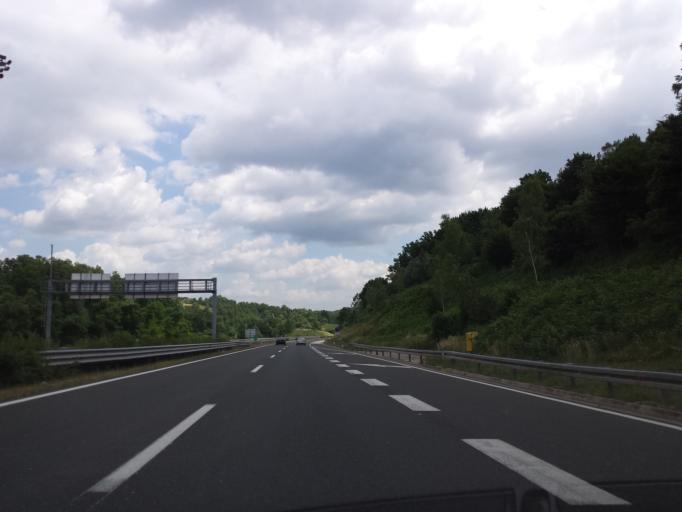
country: HR
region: Karlovacka
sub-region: Grad Karlovac
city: Karlovac
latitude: 45.4815
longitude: 15.4321
